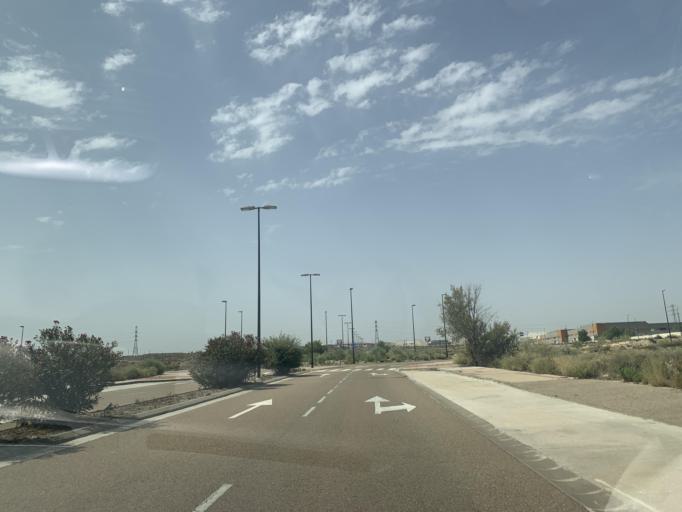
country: ES
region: Aragon
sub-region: Provincia de Zaragoza
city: Puebla de Alfinden
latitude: 41.5908
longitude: -0.8138
